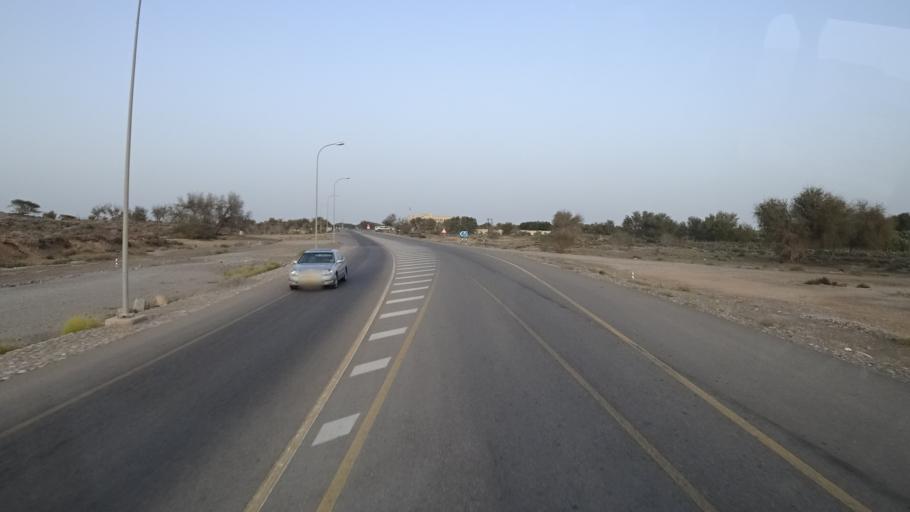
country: OM
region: Muhafazat Masqat
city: Muscat
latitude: 23.2044
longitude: 58.9533
